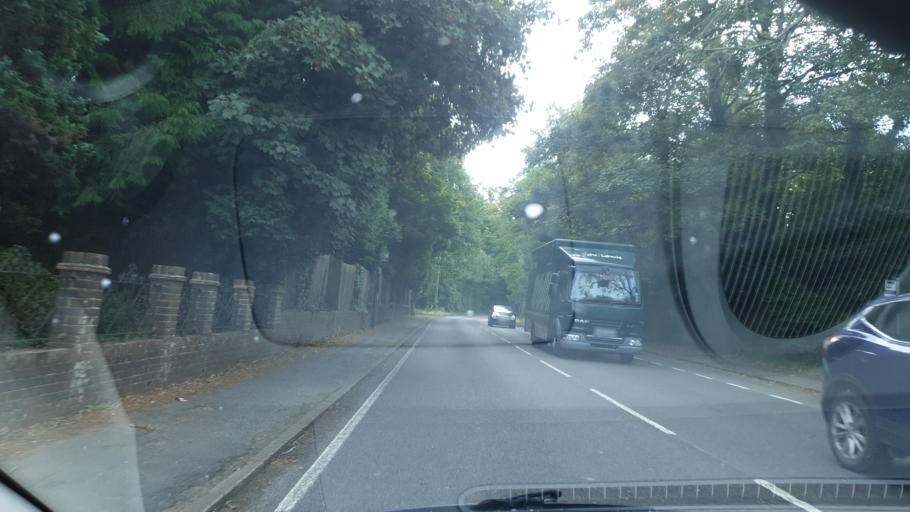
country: GB
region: England
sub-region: West Sussex
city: East Grinstead
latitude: 51.1196
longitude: 0.0097
